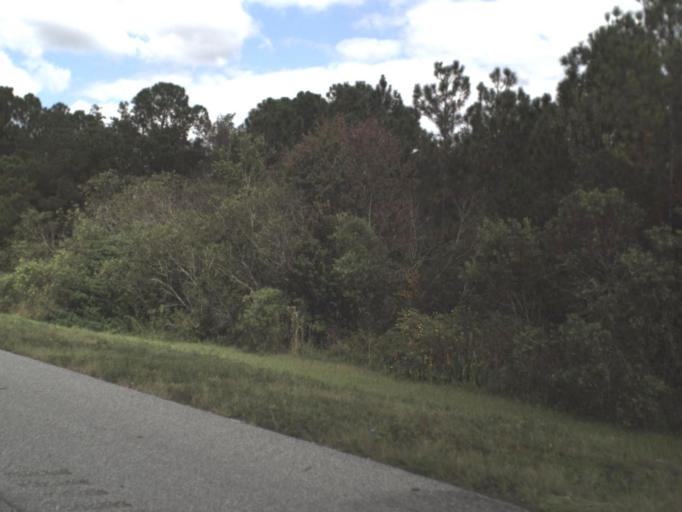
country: US
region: Florida
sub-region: Orange County
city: Tangelo Park
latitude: 28.4871
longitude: -81.4554
